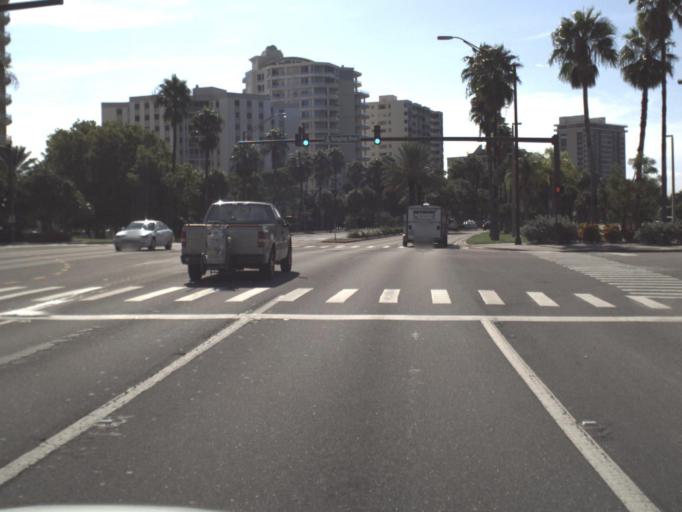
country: US
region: Florida
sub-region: Sarasota County
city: Sarasota
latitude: 27.3331
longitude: -82.5432
